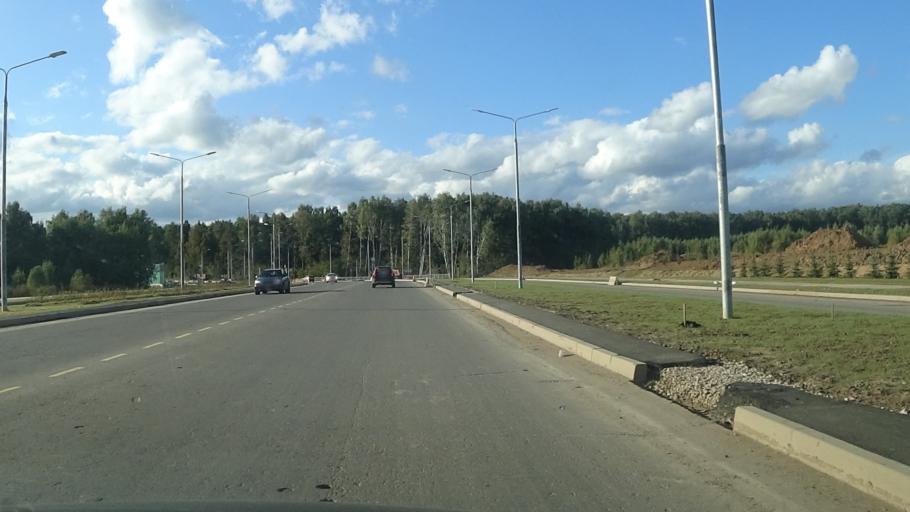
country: RU
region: Moskovskaya
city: Filimonki
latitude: 55.5670
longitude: 37.4076
